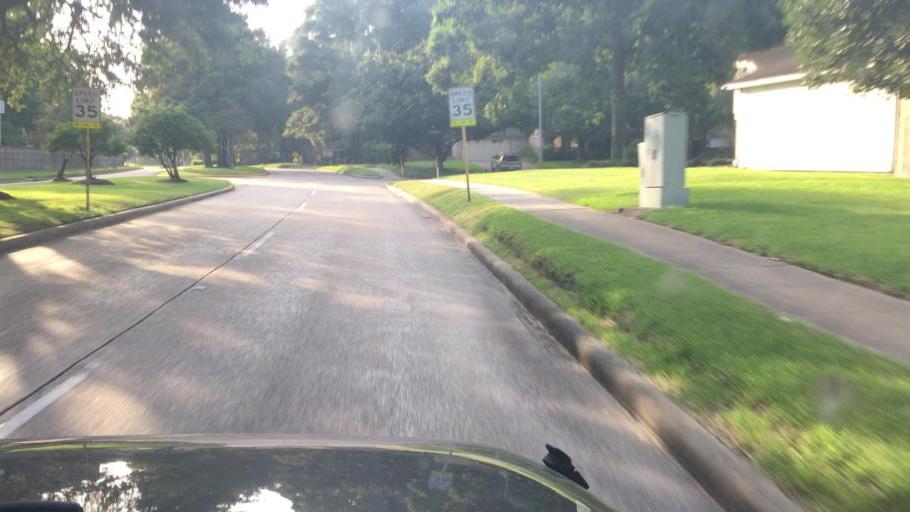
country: US
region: Texas
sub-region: Harris County
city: Atascocita
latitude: 30.0062
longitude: -95.1660
